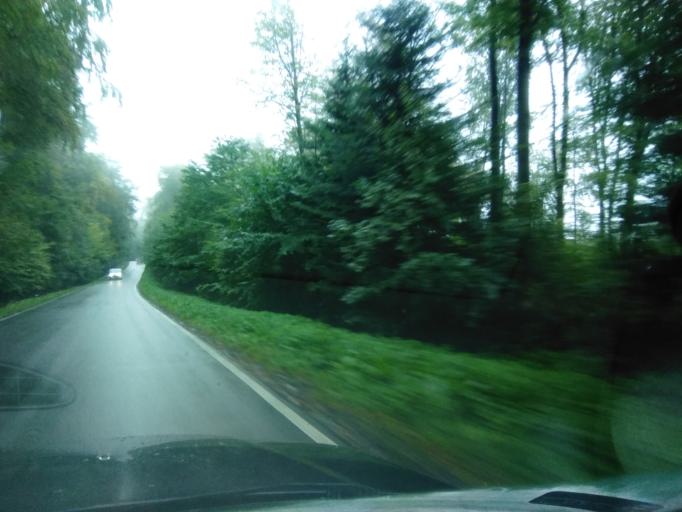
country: PL
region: Subcarpathian Voivodeship
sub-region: Powiat ropczycko-sedziszowski
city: Niedzwiada
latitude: 50.0510
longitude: 21.5342
